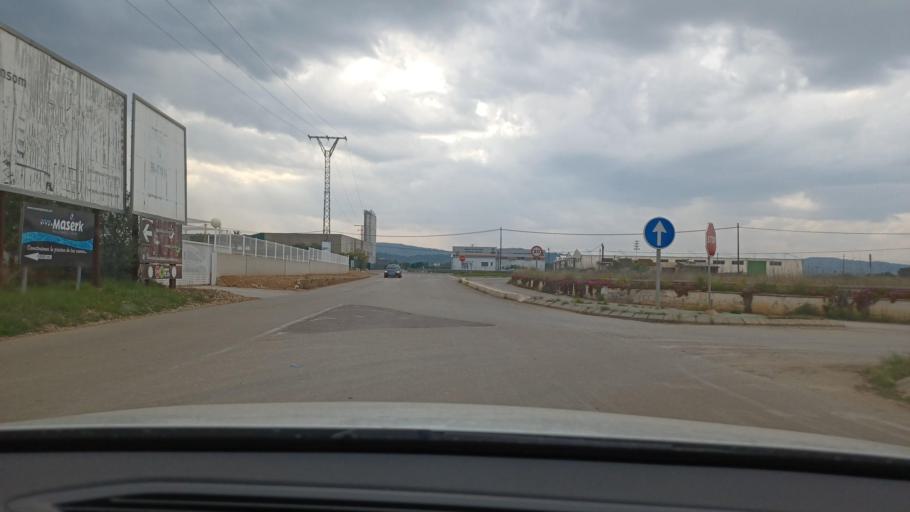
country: ES
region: Valencia
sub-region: Provincia de Castello
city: Benicarlo
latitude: 40.4093
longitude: 0.3937
